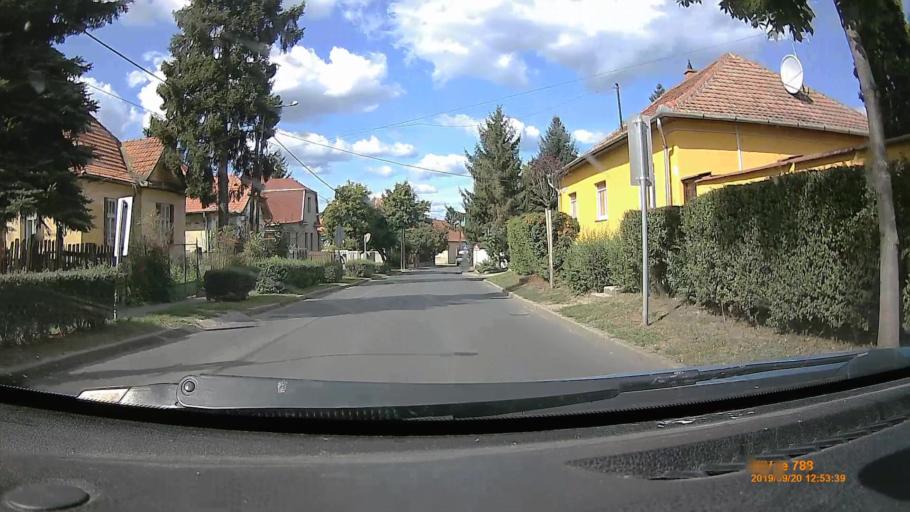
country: HU
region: Heves
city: Eger
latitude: 47.9081
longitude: 20.3797
